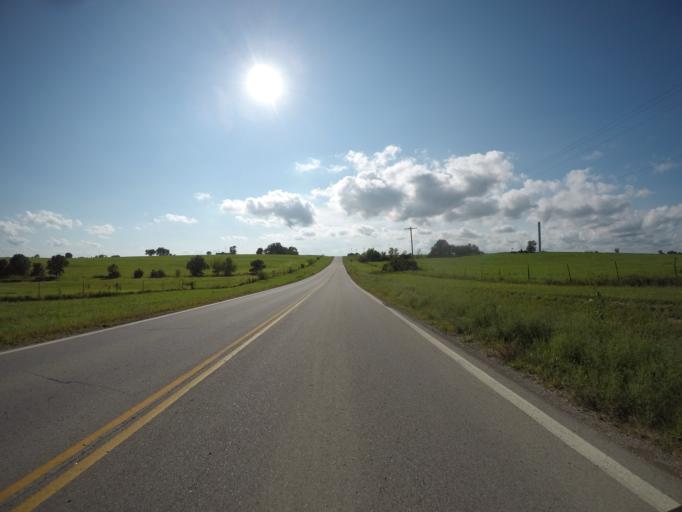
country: US
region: Kansas
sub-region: Jefferson County
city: Oskaloosa
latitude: 39.1944
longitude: -95.2231
